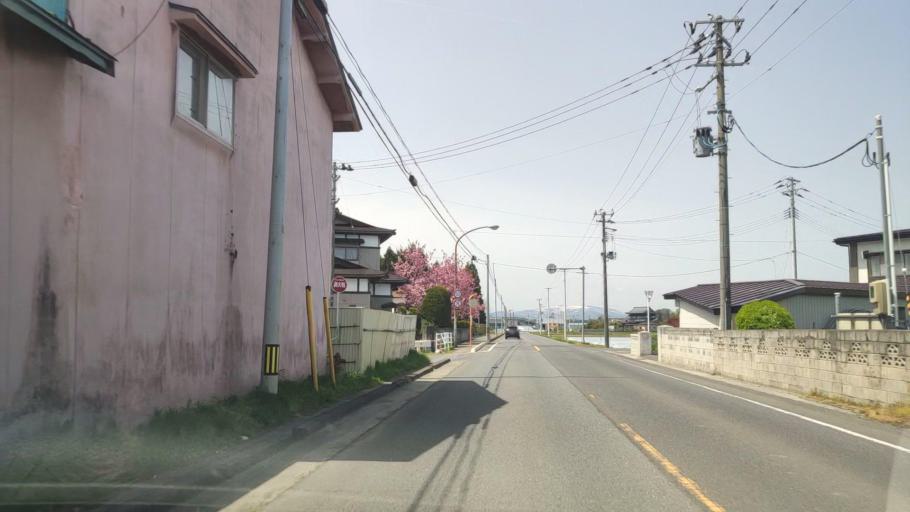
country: JP
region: Aomori
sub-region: Misawa Shi
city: Inuotose
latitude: 40.6020
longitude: 141.3016
